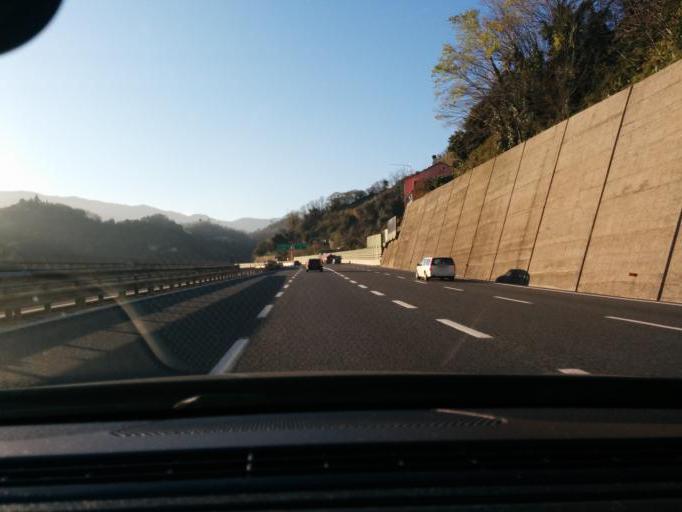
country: IT
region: Liguria
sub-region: Provincia di Genova
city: Mele
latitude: 44.4320
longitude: 8.7523
